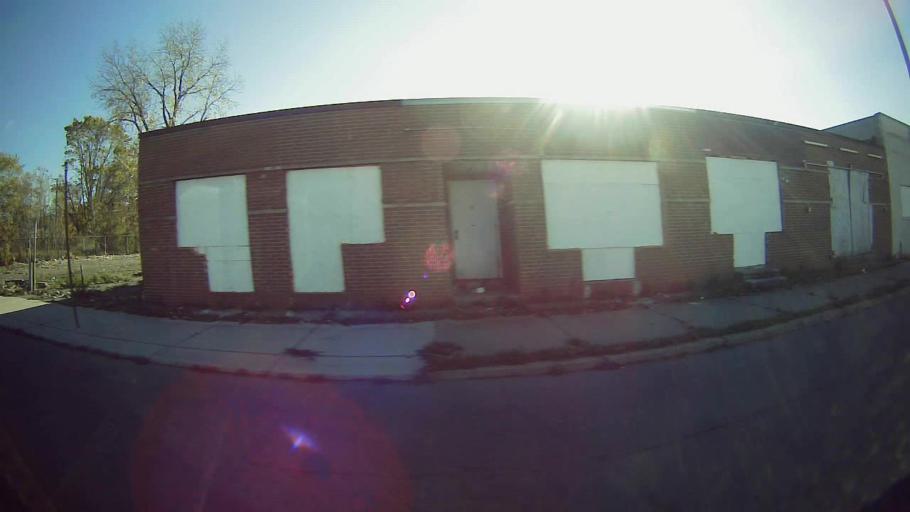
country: US
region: Michigan
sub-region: Wayne County
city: Highland Park
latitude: 42.4322
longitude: -83.1084
